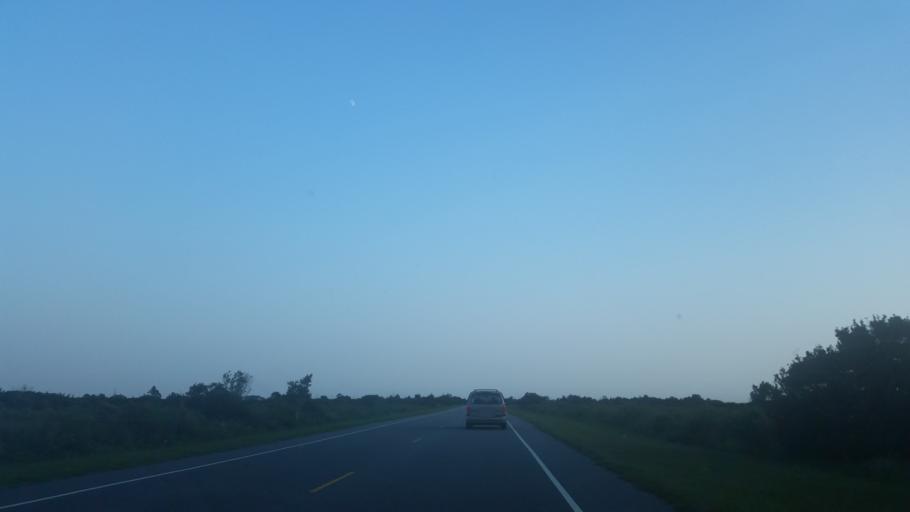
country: US
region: North Carolina
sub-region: Dare County
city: Wanchese
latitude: 35.8875
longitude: -75.5911
